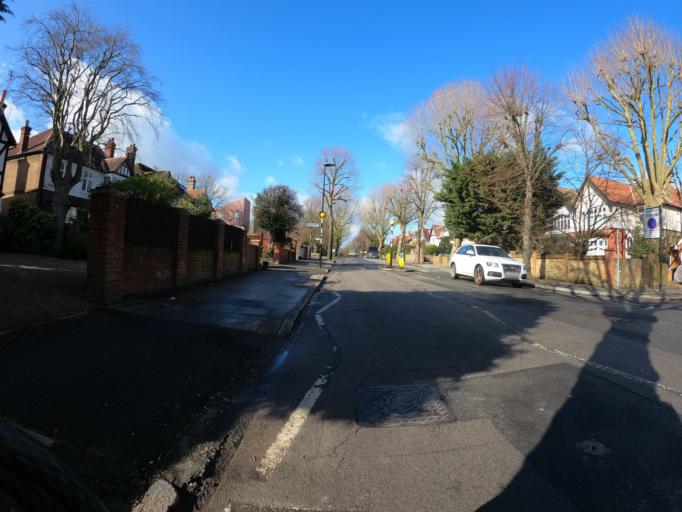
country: GB
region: England
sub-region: Greater London
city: Ealing
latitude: 51.5195
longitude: -0.3229
